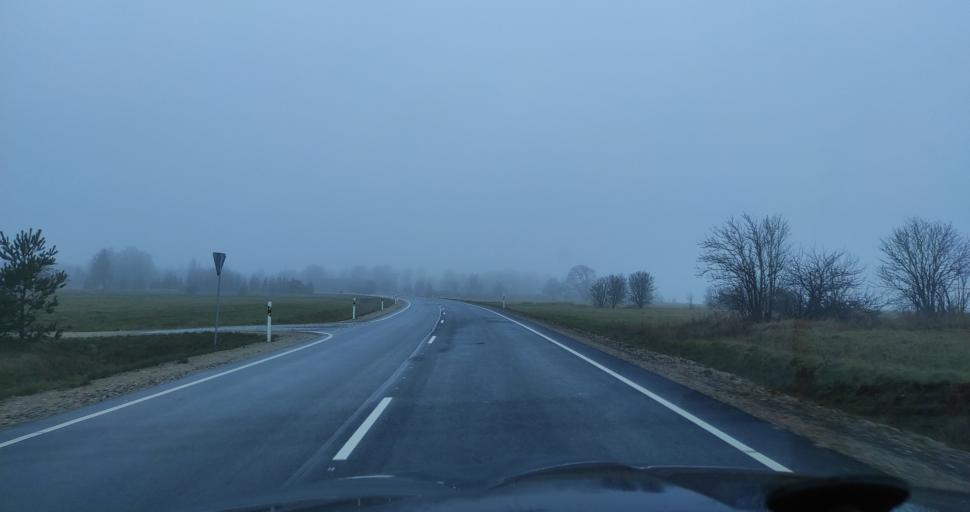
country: LV
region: Pavilostas
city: Pavilosta
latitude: 56.9181
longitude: 21.2501
